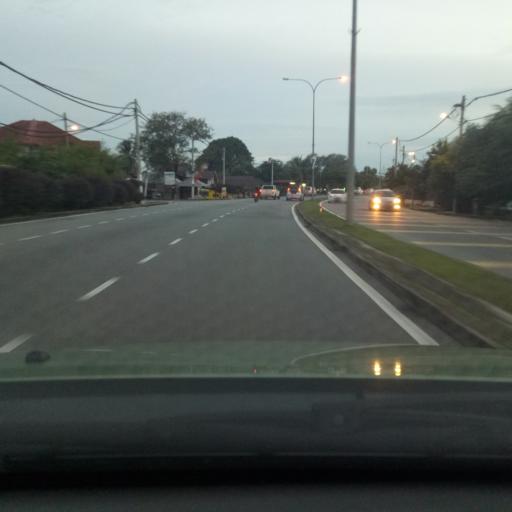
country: MY
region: Kedah
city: Alor Setar
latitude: 6.1131
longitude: 100.3752
